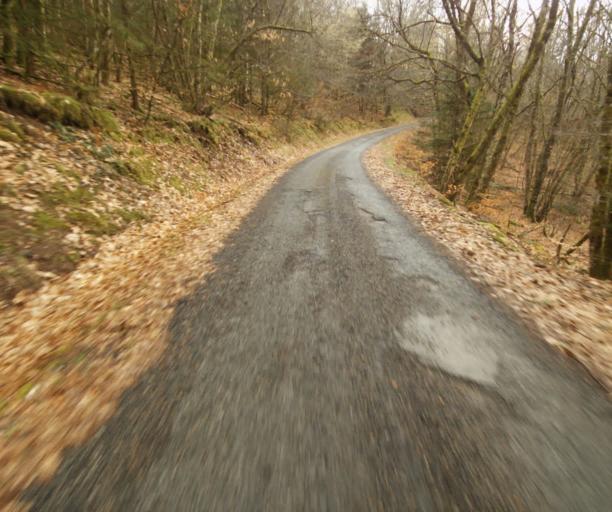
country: FR
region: Limousin
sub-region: Departement de la Correze
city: Saint-Privat
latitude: 45.2197
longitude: 2.0284
